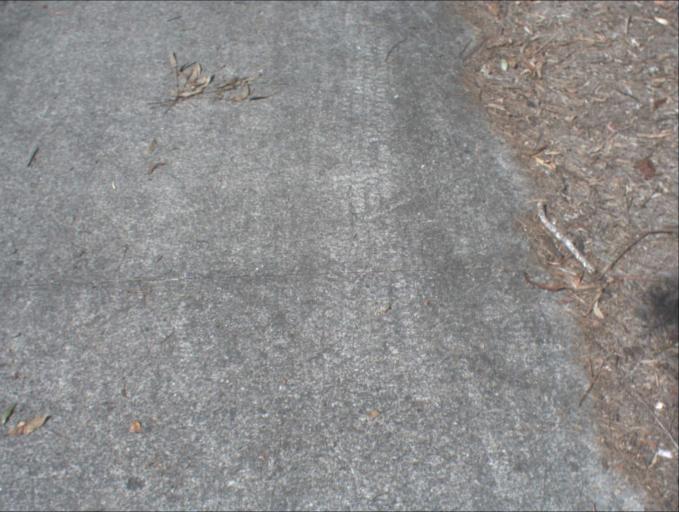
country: AU
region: Queensland
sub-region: Logan
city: Waterford West
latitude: -27.7109
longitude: 153.1513
